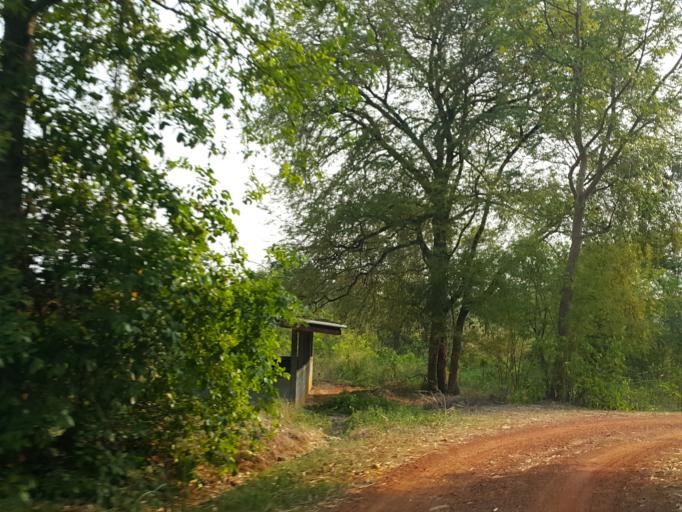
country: TH
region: Uthai Thani
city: Huai Khot
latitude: 15.3195
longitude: 99.6760
